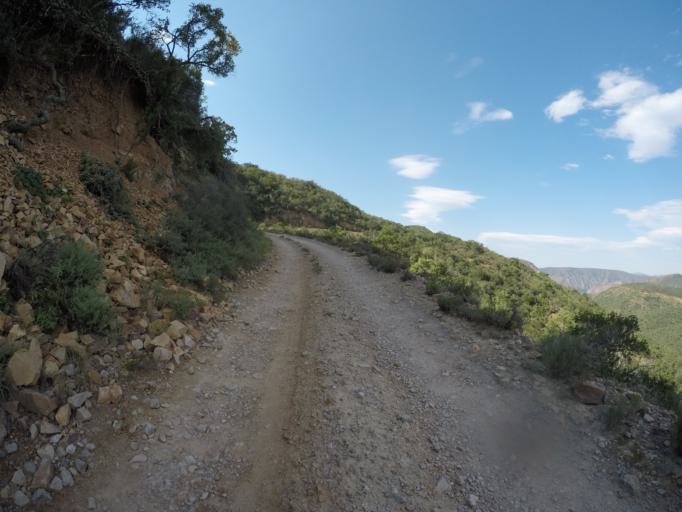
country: ZA
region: Eastern Cape
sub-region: Cacadu District Municipality
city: Kareedouw
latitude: -33.6502
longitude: 24.3492
